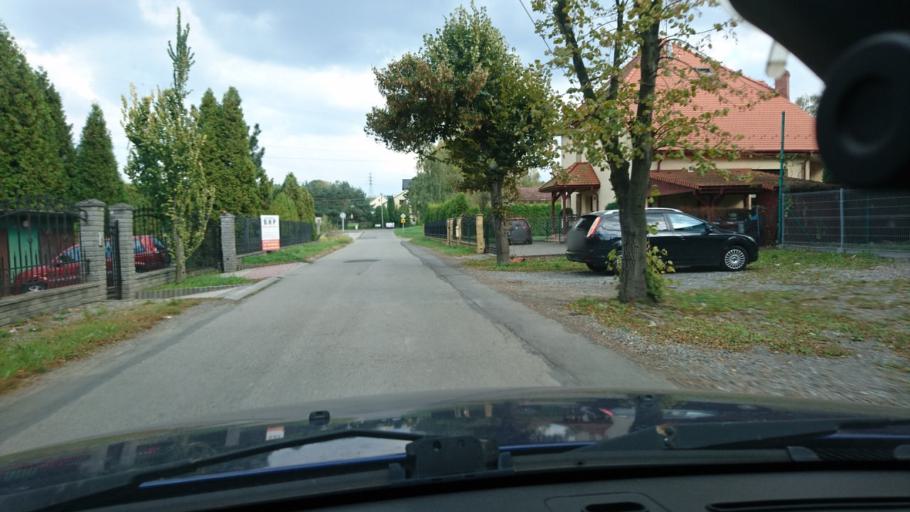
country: PL
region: Silesian Voivodeship
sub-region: Bielsko-Biala
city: Bielsko-Biala
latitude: 49.8454
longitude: 19.0531
